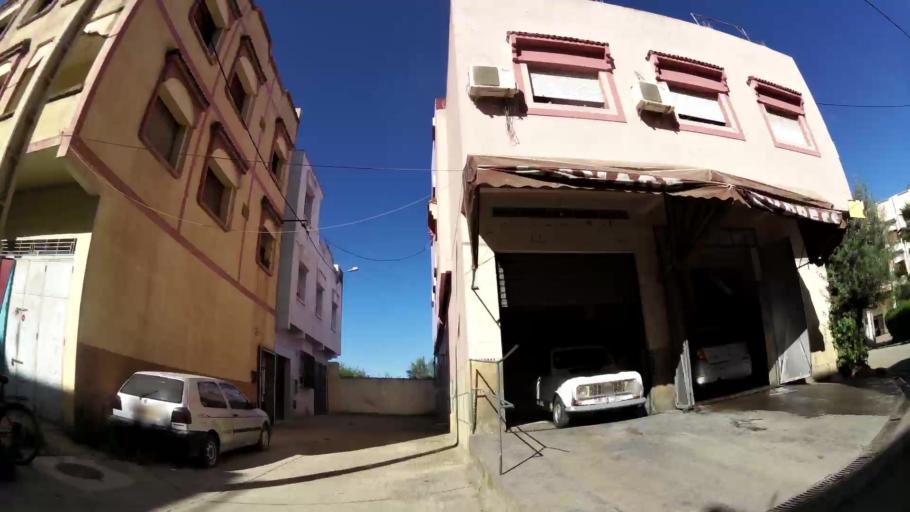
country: MA
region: Meknes-Tafilalet
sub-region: Meknes
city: Meknes
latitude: 33.8959
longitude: -5.4997
